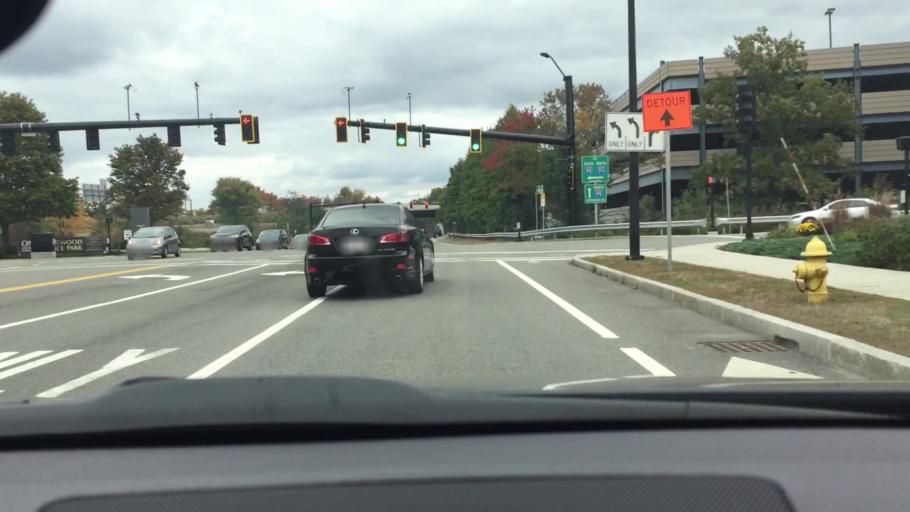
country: US
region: Massachusetts
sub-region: Norfolk County
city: Dedham
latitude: 42.2108
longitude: -71.1499
